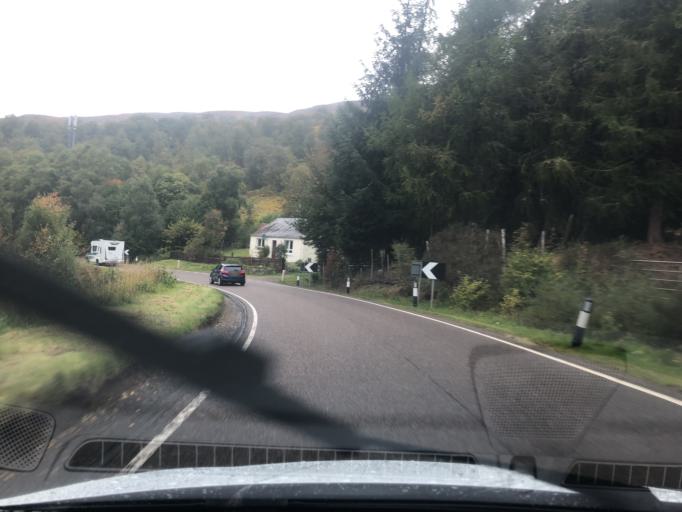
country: GB
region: Scotland
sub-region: Highland
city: Kingussie
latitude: 56.9821
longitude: -4.3694
